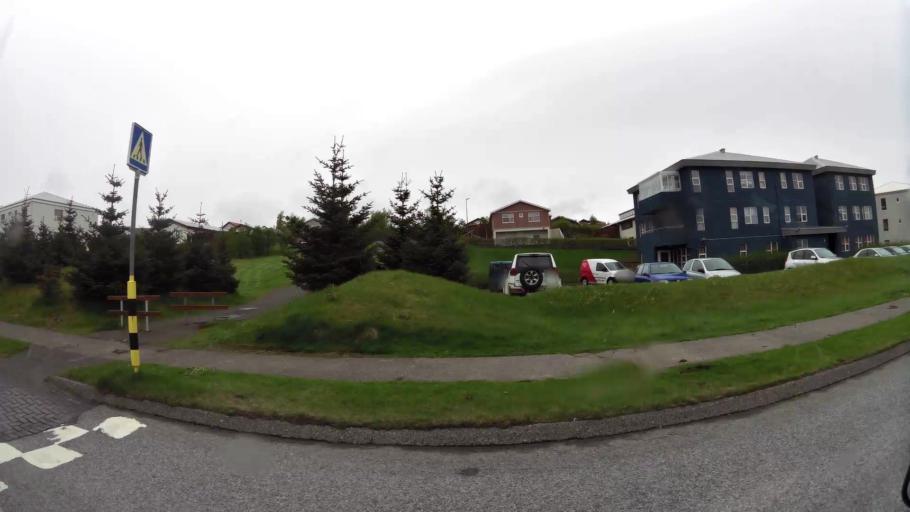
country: IS
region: Capital Region
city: Hafnarfjoerdur
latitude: 64.0618
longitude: -21.9341
